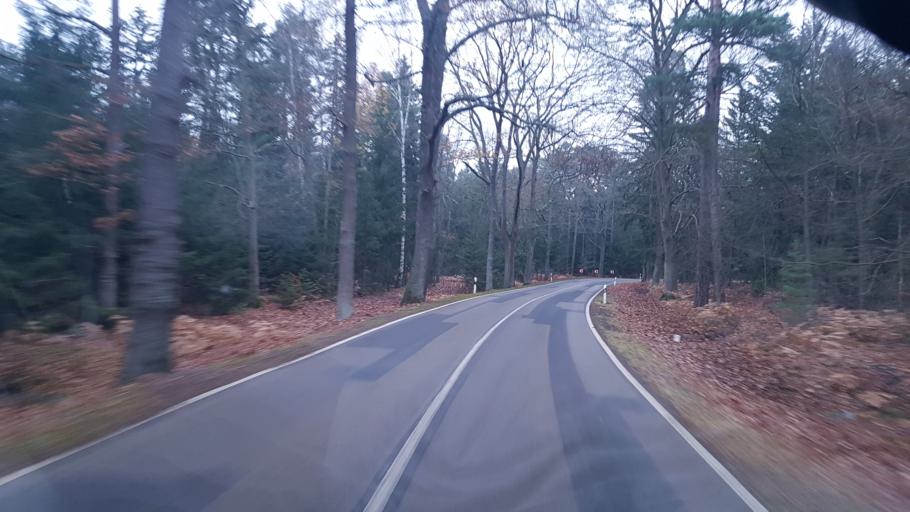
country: DE
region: Brandenburg
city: Drachhausen
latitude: 51.8736
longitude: 14.2788
